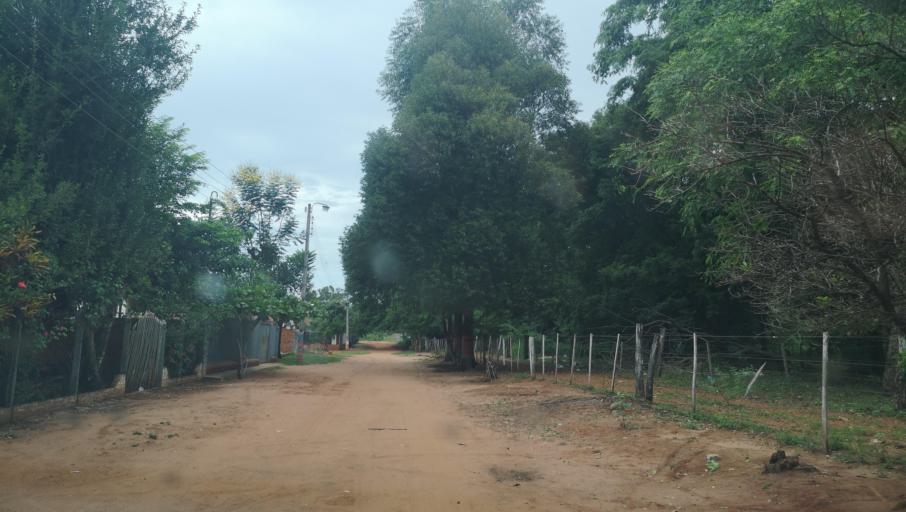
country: PY
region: San Pedro
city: Capiibary
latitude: -24.7415
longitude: -56.0358
